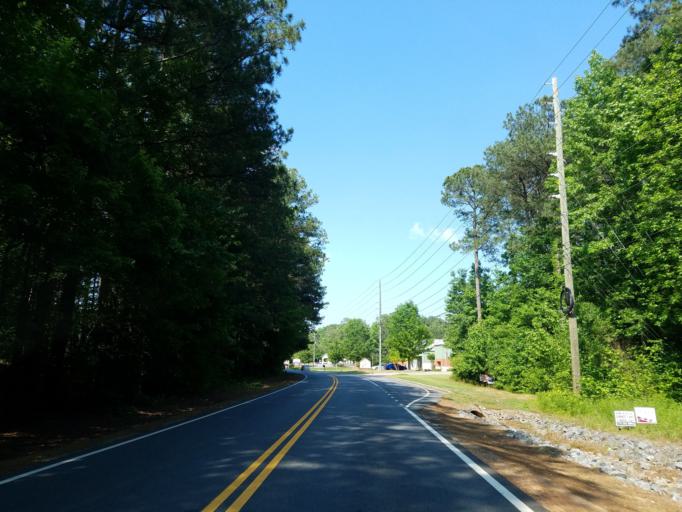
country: US
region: Georgia
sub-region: Cherokee County
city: Holly Springs
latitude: 34.1825
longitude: -84.5464
